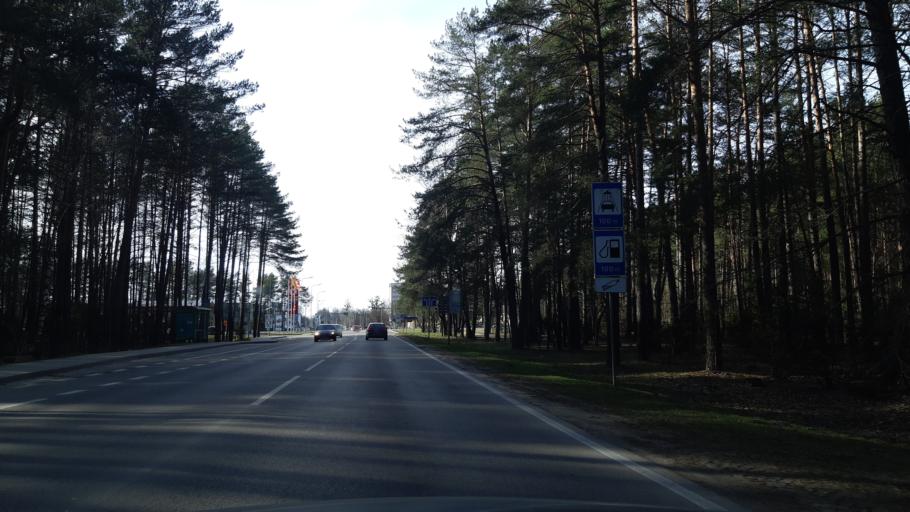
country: LT
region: Alytaus apskritis
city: Druskininkai
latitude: 54.0097
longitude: 23.9957
